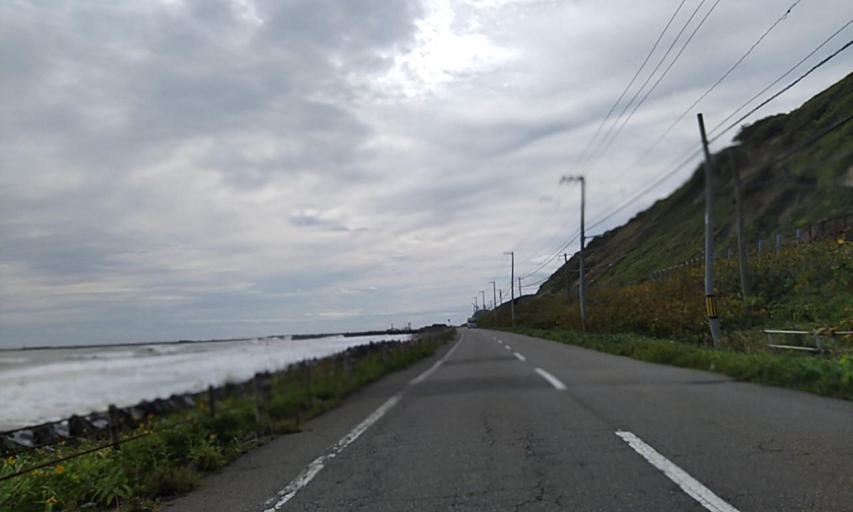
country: JP
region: Hokkaido
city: Kushiro
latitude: 42.8115
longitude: 143.8263
